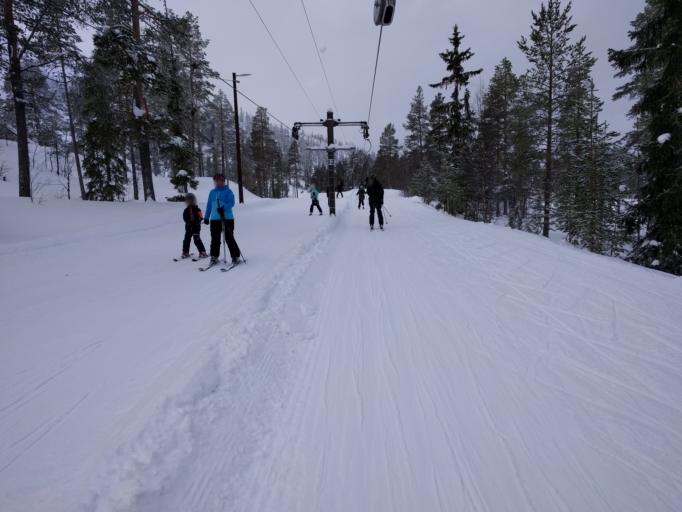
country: NO
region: Hedmark
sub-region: Trysil
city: Innbygda
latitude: 61.1734
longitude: 12.9840
